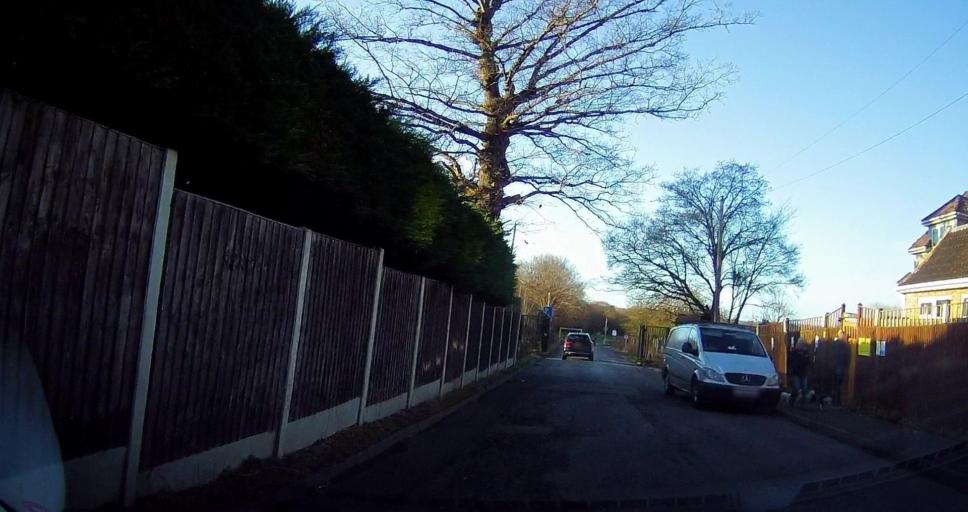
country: GB
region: England
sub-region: Greater London
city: Bromley
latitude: 51.3907
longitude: 0.0335
